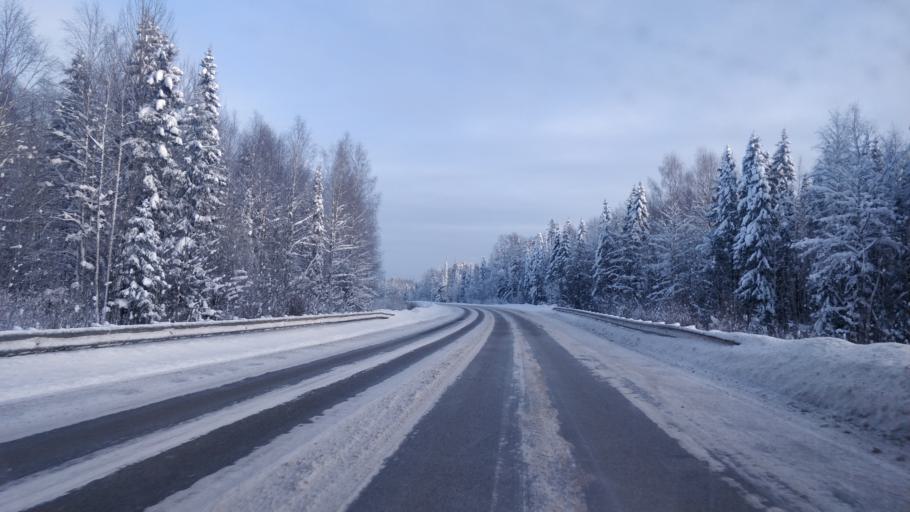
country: RU
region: Perm
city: Polazna
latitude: 58.2994
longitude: 56.5635
